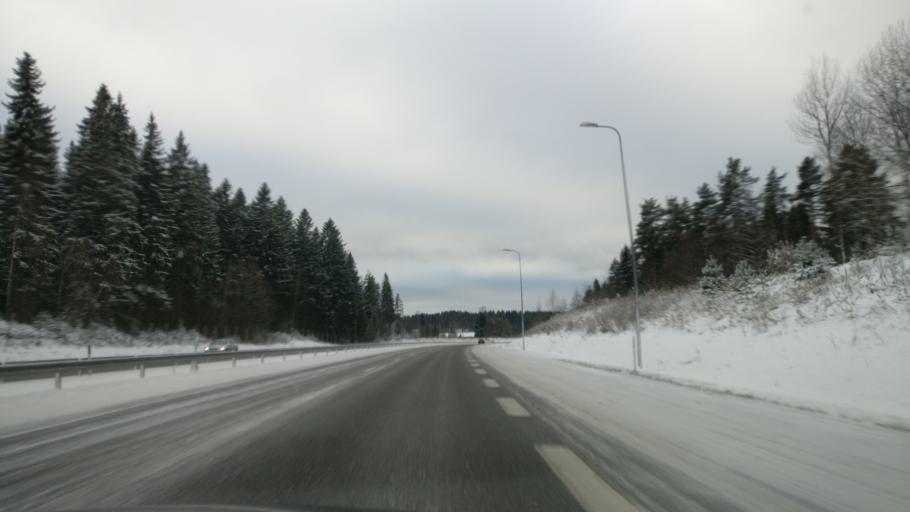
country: FI
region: Paijanne Tavastia
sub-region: Lahti
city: Lahti
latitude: 60.9947
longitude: 25.7772
